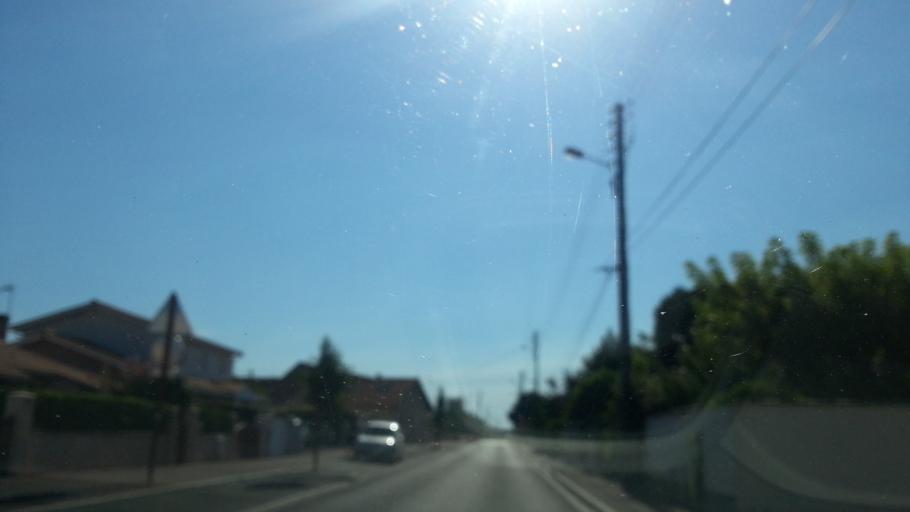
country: FR
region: Aquitaine
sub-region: Departement de la Gironde
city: Villenave-d'Ornon
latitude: 44.7678
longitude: -0.5727
